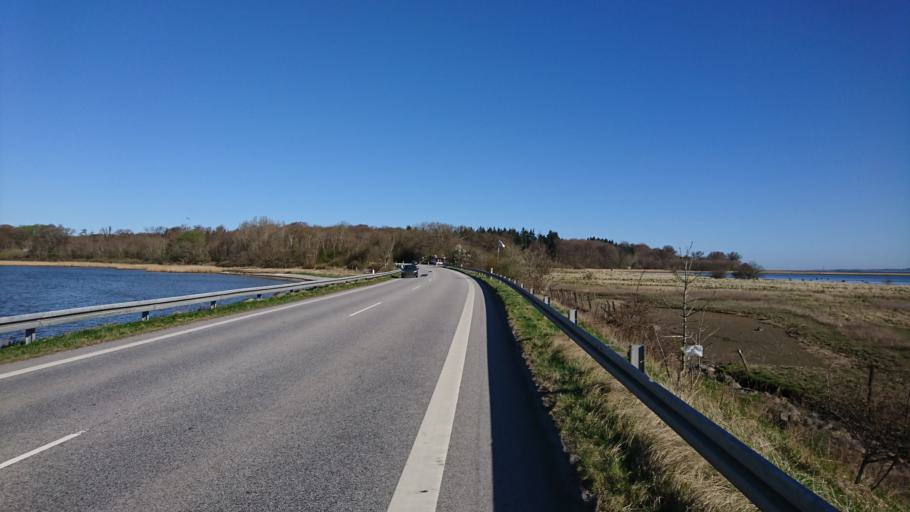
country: DK
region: Zealand
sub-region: Lejre Kommune
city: Ejby
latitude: 55.6794
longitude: 11.8044
